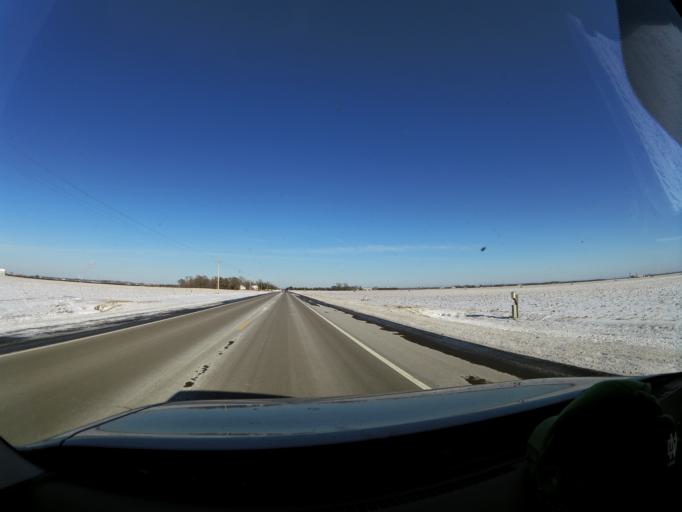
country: US
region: Minnesota
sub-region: Dakota County
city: Hastings
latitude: 44.6822
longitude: -92.9166
